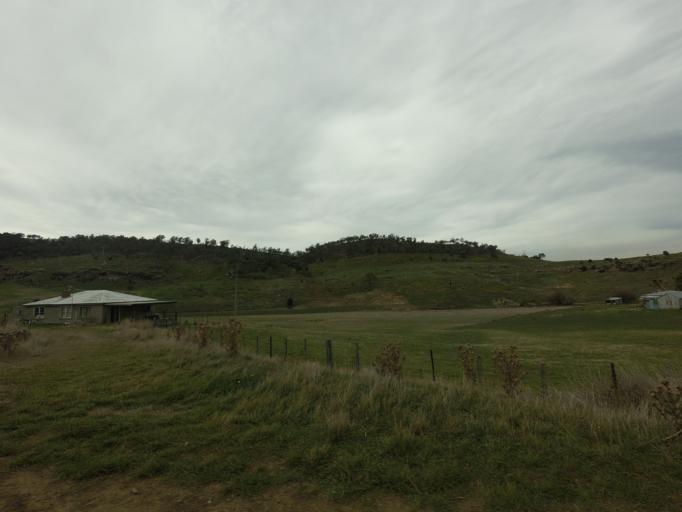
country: AU
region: Tasmania
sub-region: Derwent Valley
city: New Norfolk
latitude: -42.4042
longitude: 146.9203
